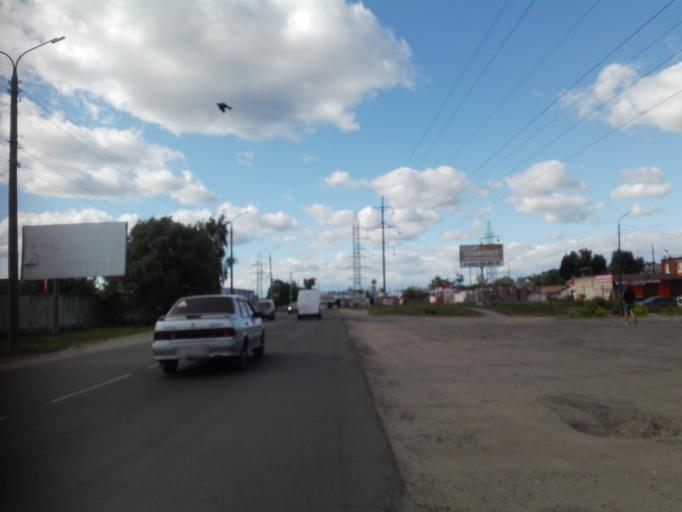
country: RU
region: Orjol
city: Orel
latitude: 52.9436
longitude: 36.0321
